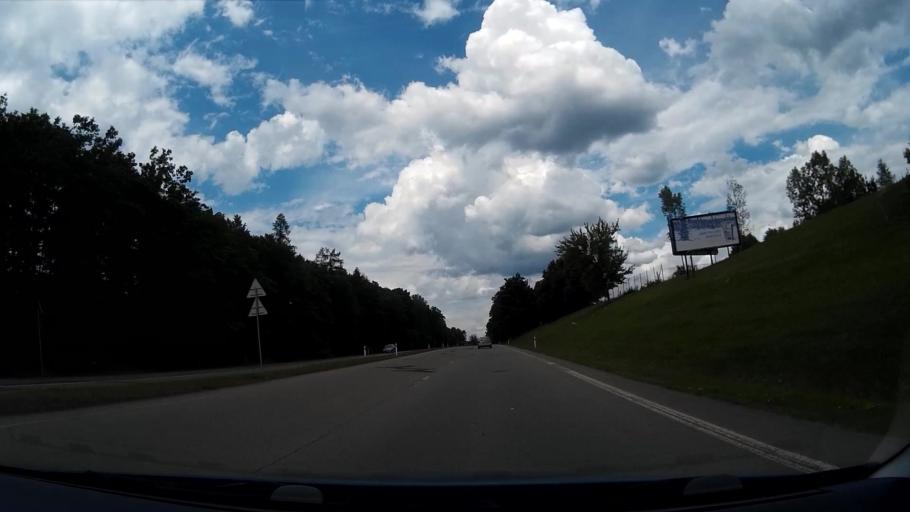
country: CZ
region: South Moravian
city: Troubsko
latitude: 49.2163
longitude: 16.5217
